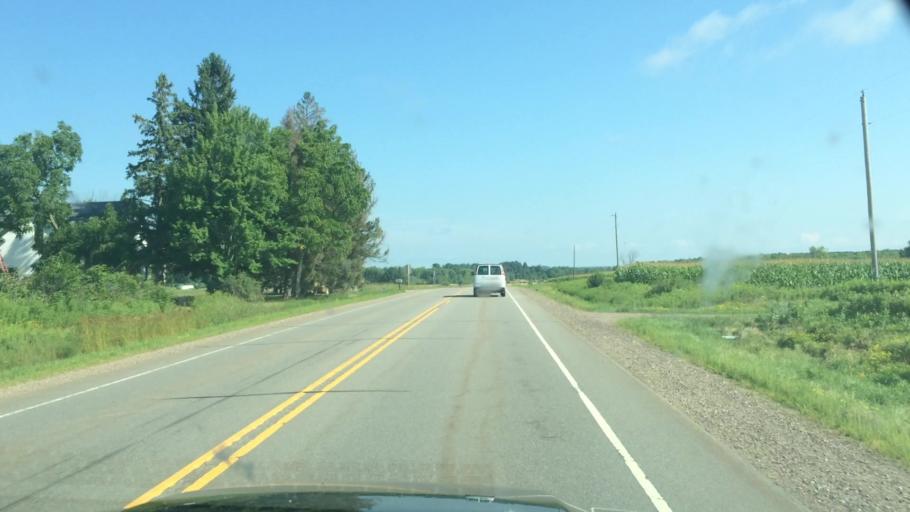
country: US
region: Wisconsin
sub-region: Lincoln County
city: Merrill
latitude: 45.1522
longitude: -89.4668
